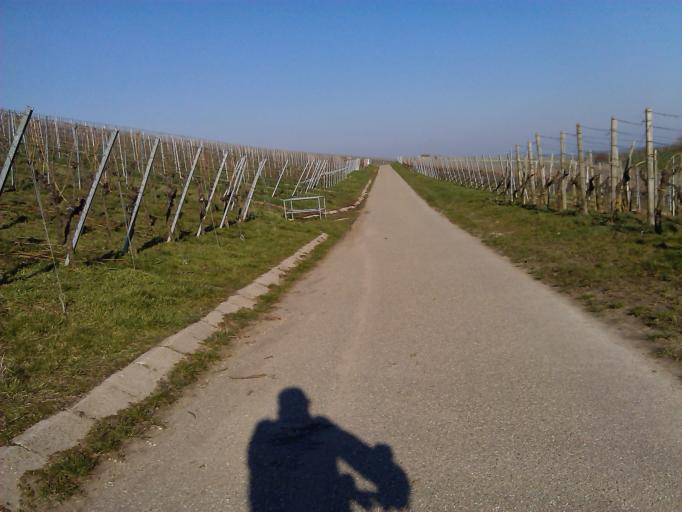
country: DE
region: Baden-Wuerttemberg
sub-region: Regierungsbezirk Stuttgart
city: Leingarten
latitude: 49.1238
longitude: 9.1049
